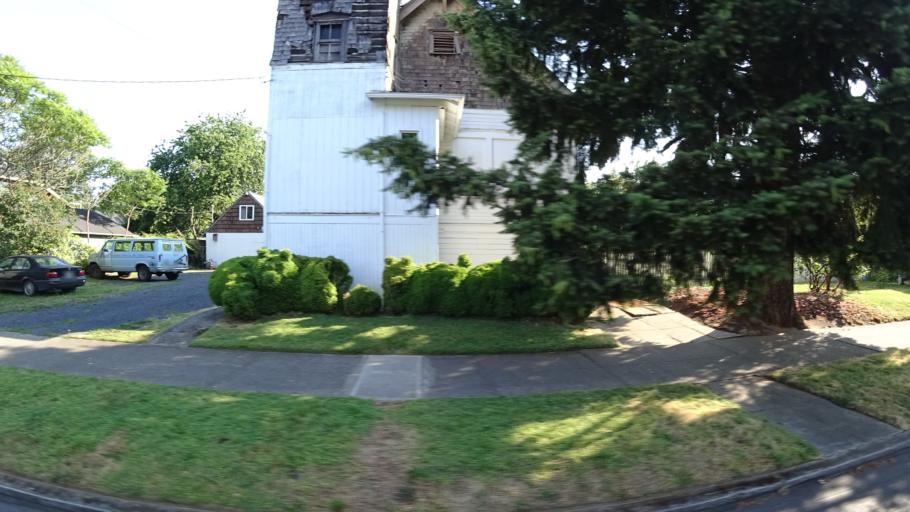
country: US
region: Oregon
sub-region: Washington County
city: West Haven
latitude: 45.5914
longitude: -122.7513
